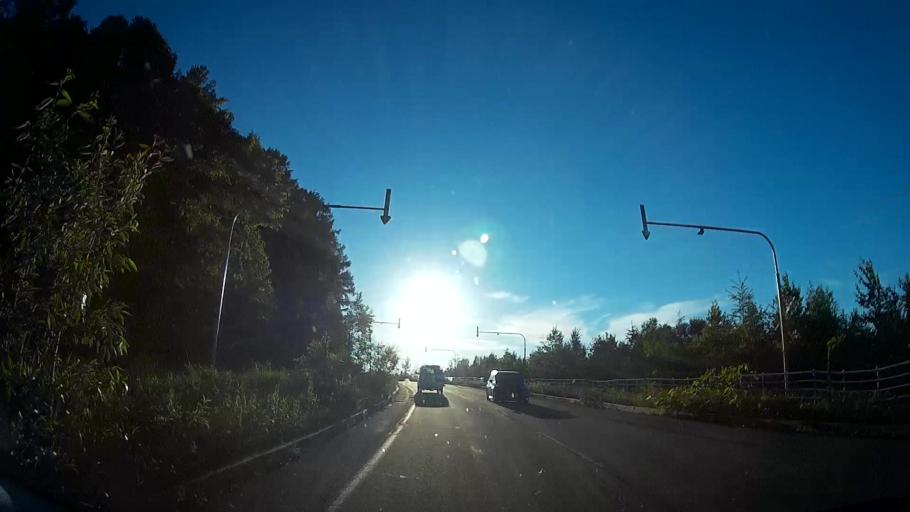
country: JP
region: Hokkaido
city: Otaru
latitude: 43.1673
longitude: 141.0213
